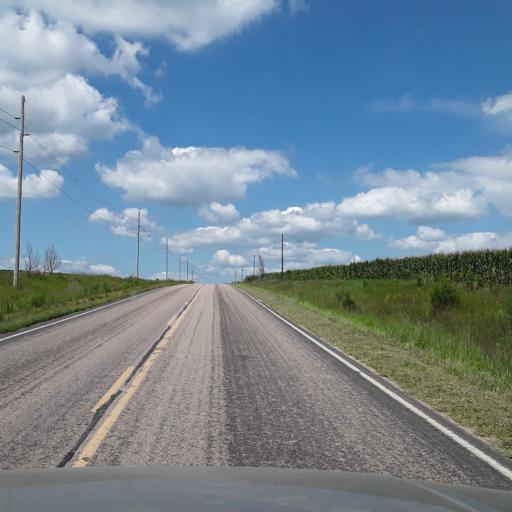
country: US
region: Nebraska
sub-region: Nance County
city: Genoa
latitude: 41.5165
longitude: -97.6960
